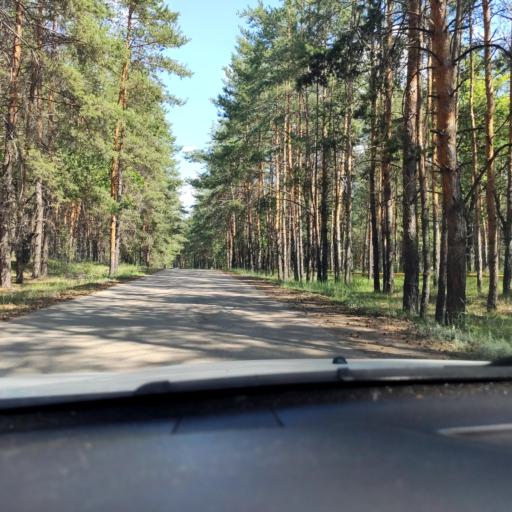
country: RU
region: Samara
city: Pribrezhnyy
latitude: 53.4706
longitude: 49.8113
